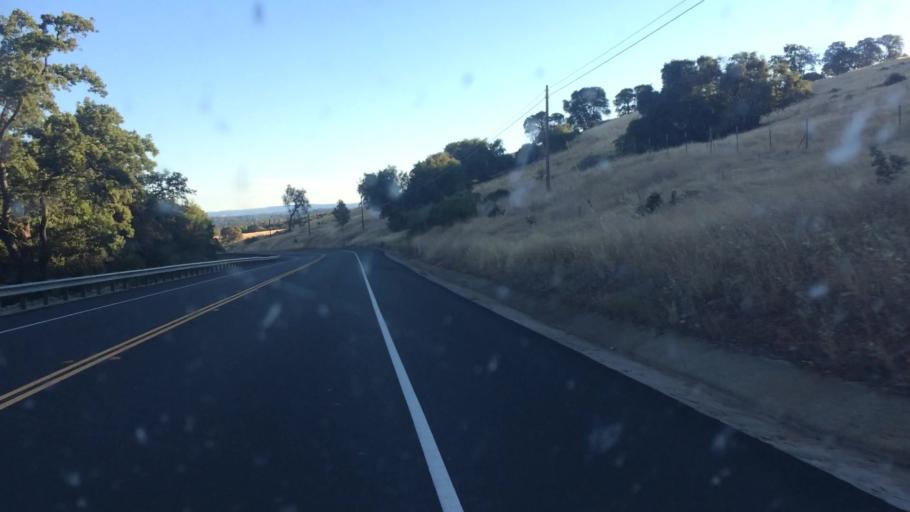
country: US
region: California
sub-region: El Dorado County
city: Deer Park
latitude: 38.6469
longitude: -120.8509
